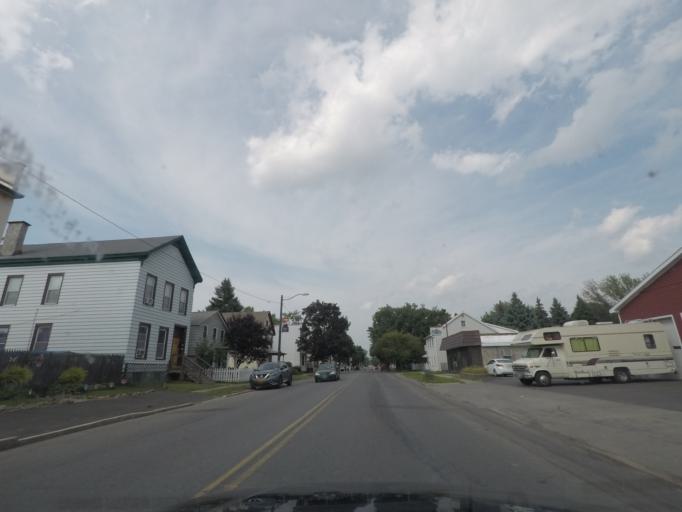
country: US
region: New York
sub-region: Saratoga County
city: Waterford
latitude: 42.7762
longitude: -73.6727
